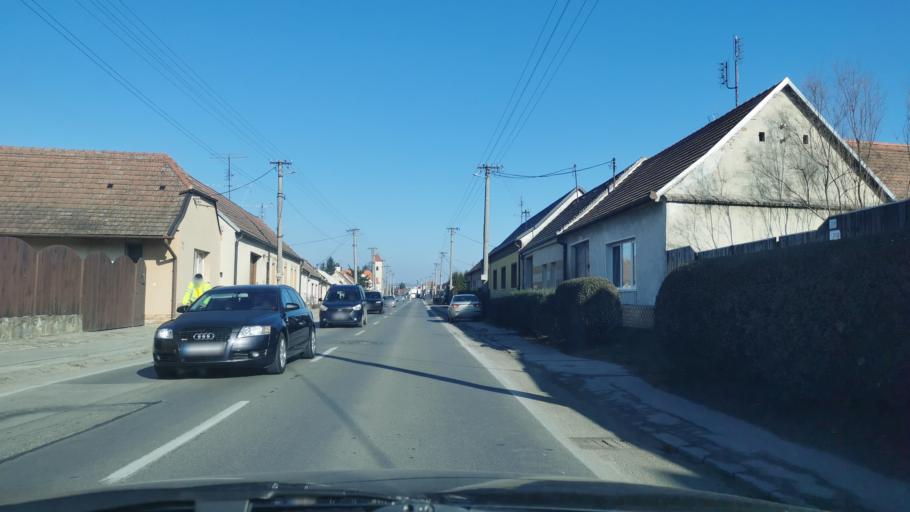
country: SK
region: Trnavsky
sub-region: Okres Senica
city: Senica
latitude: 48.6768
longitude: 17.3347
